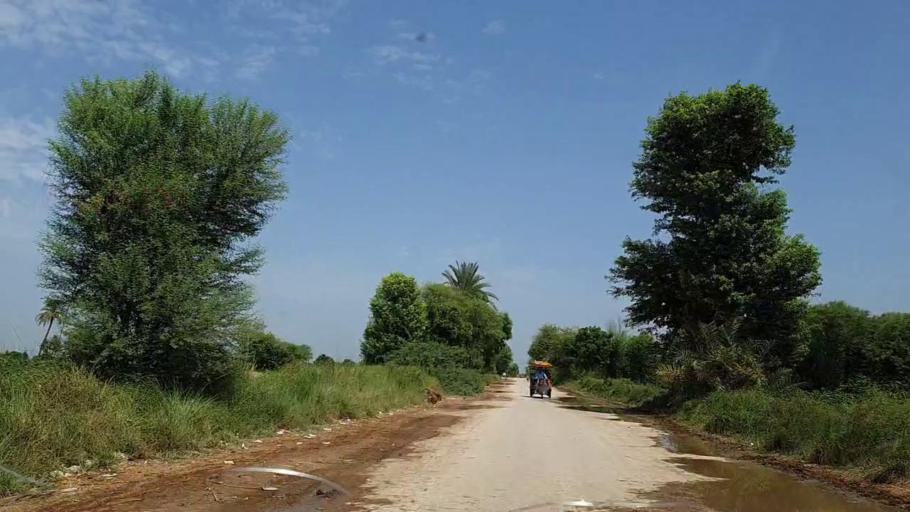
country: PK
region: Sindh
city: Naushahro Firoz
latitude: 26.8339
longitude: 68.1306
